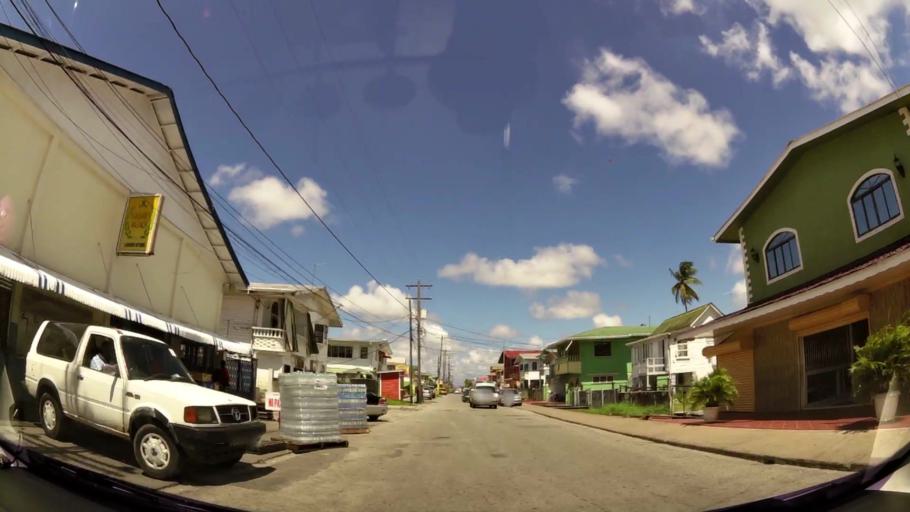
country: GY
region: Demerara-Mahaica
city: Georgetown
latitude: 6.8036
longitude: -58.1553
